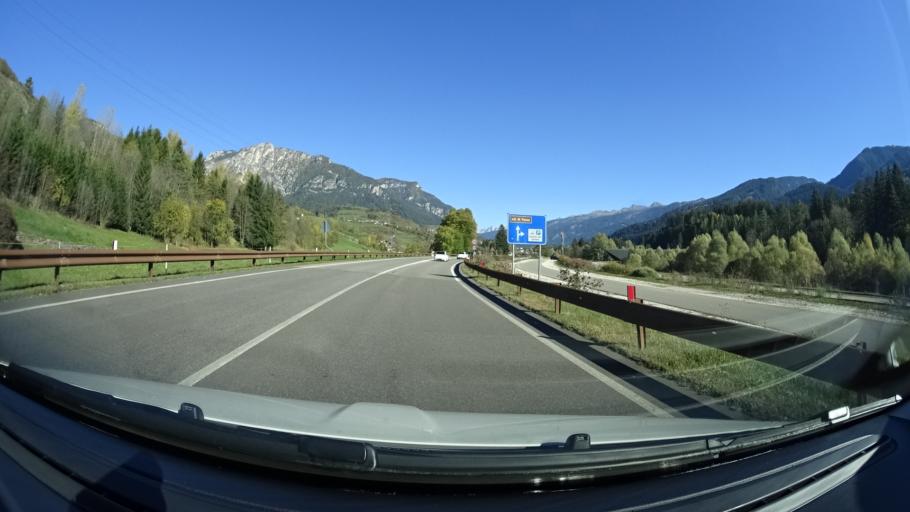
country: IT
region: Trentino-Alto Adige
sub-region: Provincia di Trento
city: Cavalese
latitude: 46.2844
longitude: 11.4683
